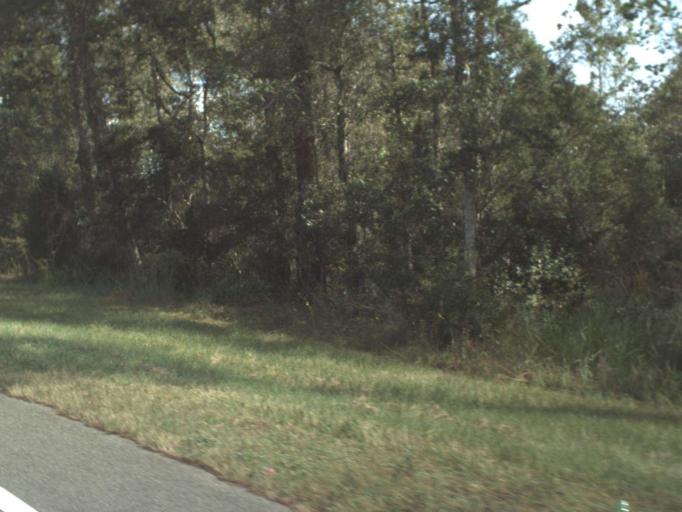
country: US
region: Florida
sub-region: Walton County
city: DeFuniak Springs
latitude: 30.8275
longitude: -86.1208
